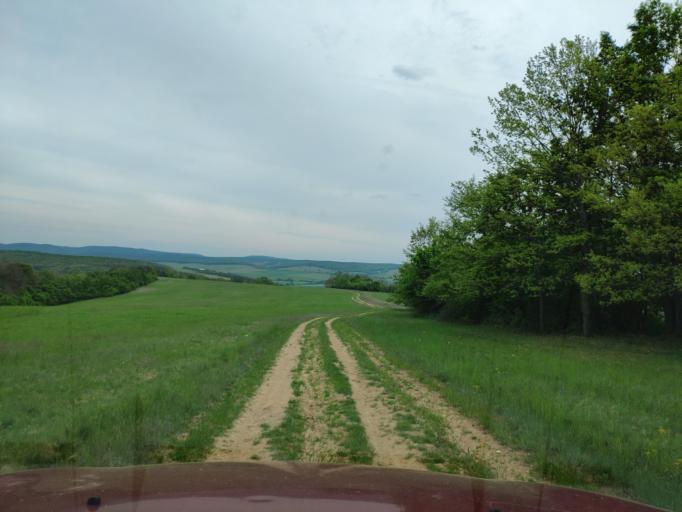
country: HU
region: Borsod-Abauj-Zemplen
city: Putnok
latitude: 48.4917
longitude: 20.3219
